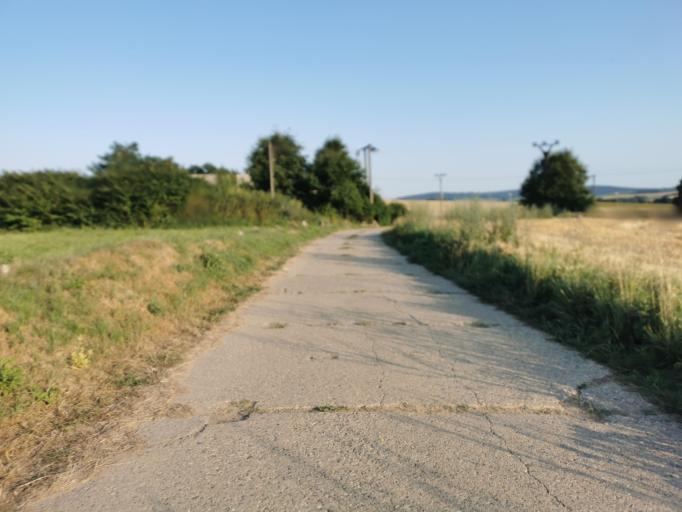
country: SK
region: Trnavsky
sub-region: Okres Skalica
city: Skalica
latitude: 48.7855
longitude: 17.2789
